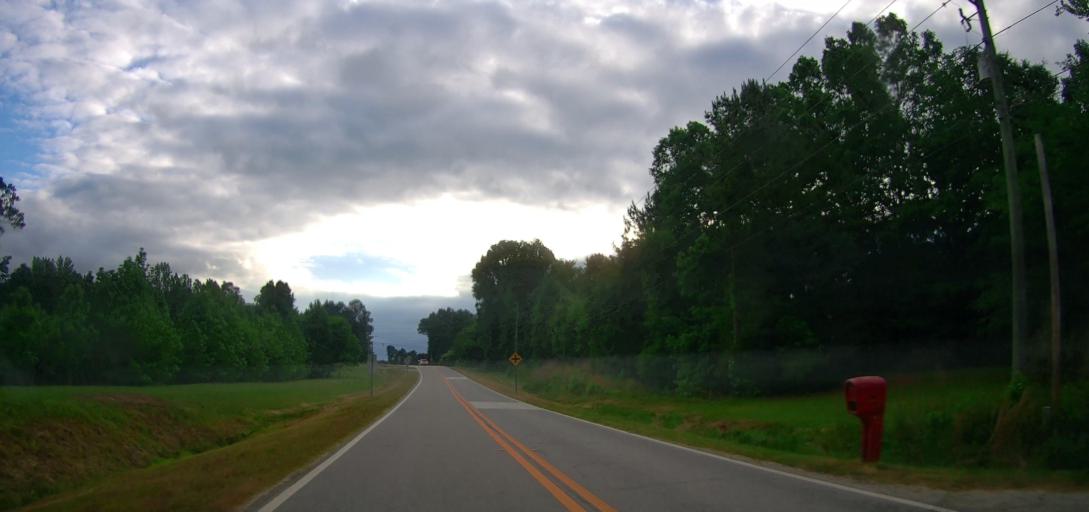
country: US
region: Georgia
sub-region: Oconee County
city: Watkinsville
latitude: 33.8437
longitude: -83.4455
